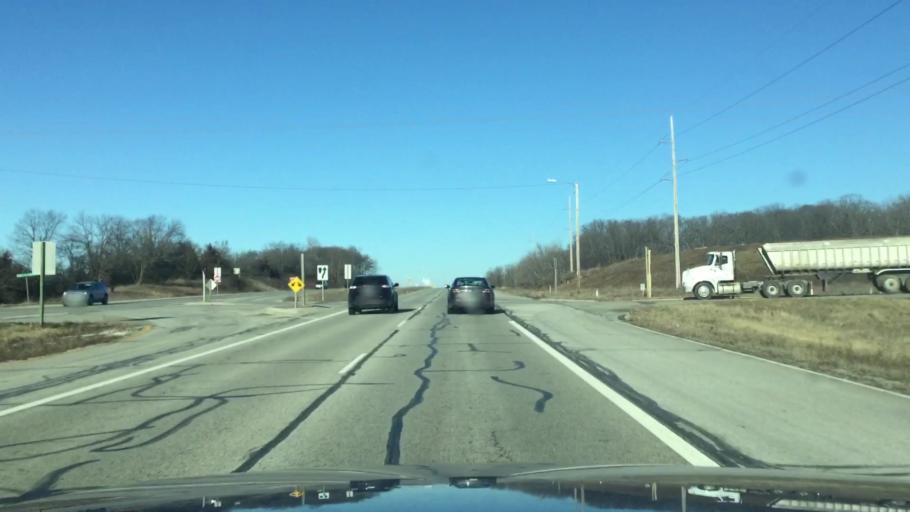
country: US
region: Wisconsin
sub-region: Racine County
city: Rochester
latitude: 42.7354
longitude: -88.2180
